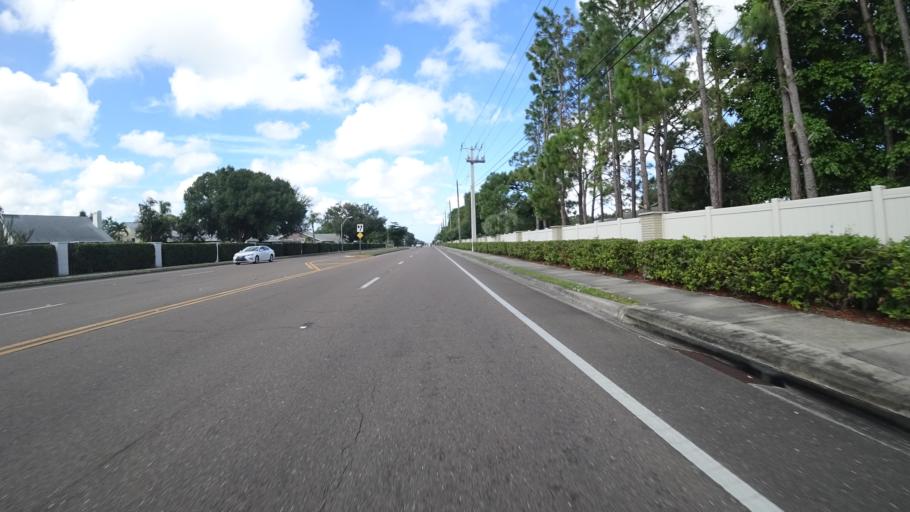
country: US
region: Florida
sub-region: Sarasota County
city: North Sarasota
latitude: 27.4035
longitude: -82.5075
